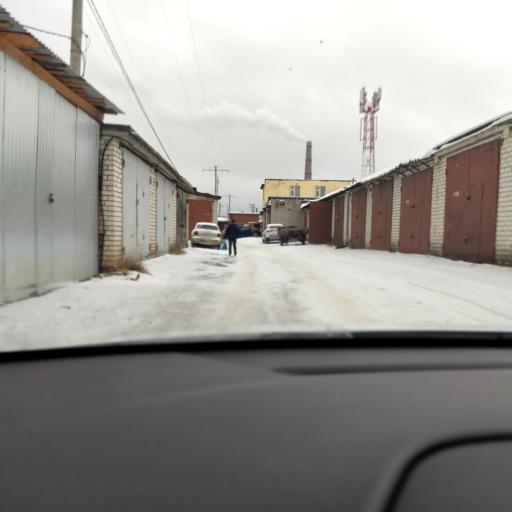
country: RU
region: Tatarstan
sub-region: Gorod Kazan'
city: Kazan
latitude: 55.7595
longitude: 49.1991
